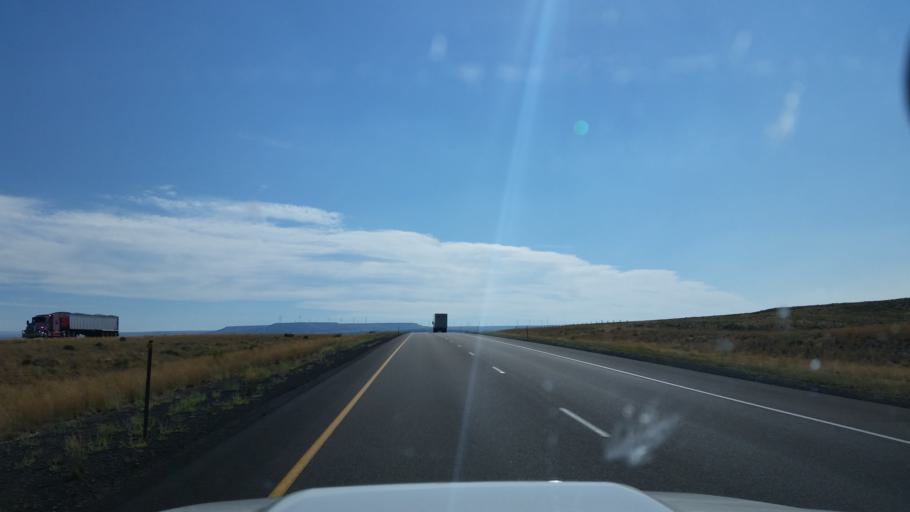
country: US
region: Wyoming
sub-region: Uinta County
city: Mountain View
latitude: 41.3487
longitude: -110.3840
